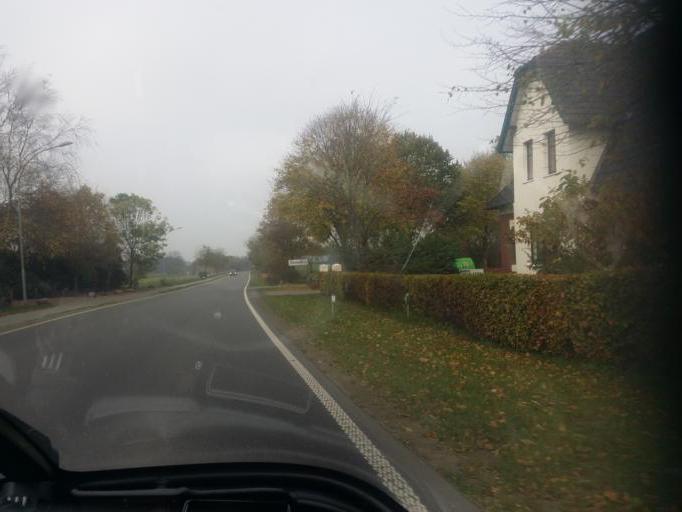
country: DE
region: Schleswig-Holstein
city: Bordelum
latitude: 54.6320
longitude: 8.9365
